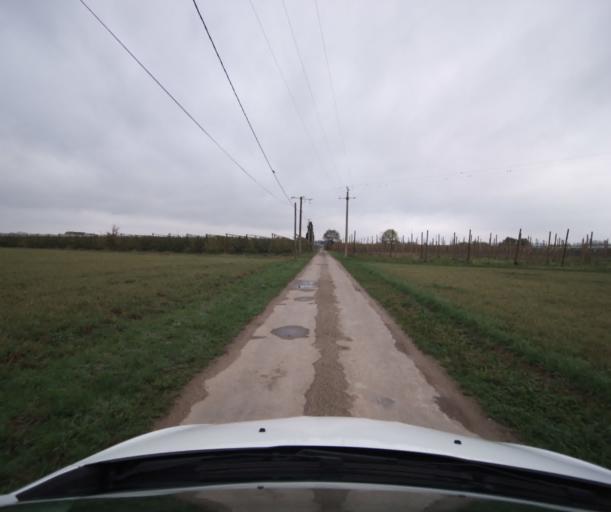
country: FR
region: Midi-Pyrenees
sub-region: Departement du Tarn-et-Garonne
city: Moissac
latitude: 44.0794
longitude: 1.1264
